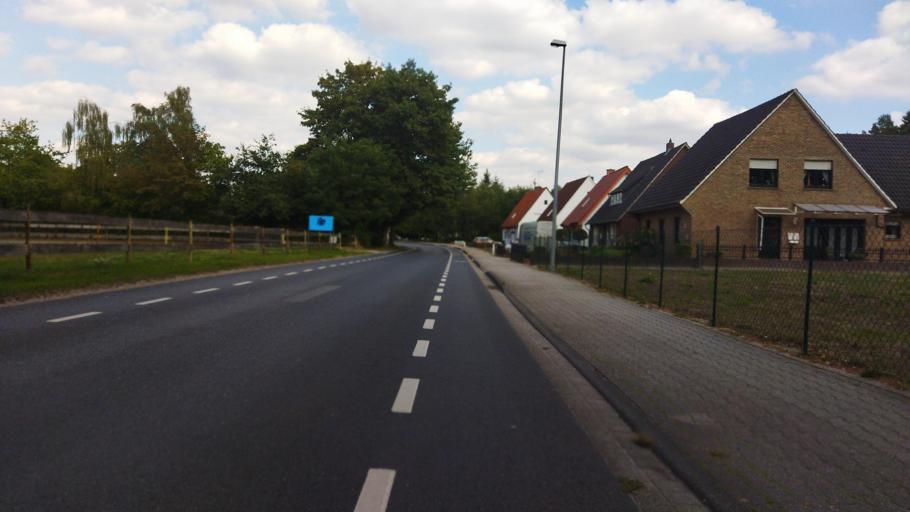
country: DE
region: Lower Saxony
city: Haren
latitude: 52.7937
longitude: 7.2660
